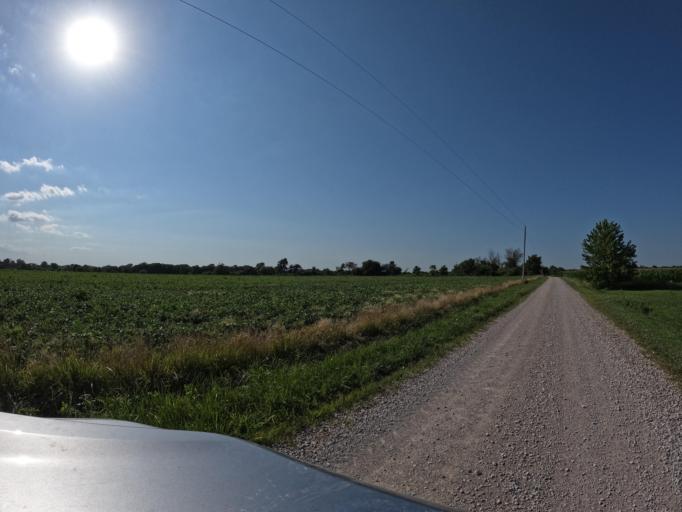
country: US
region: Iowa
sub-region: Appanoose County
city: Centerville
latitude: 40.7235
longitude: -93.0158
